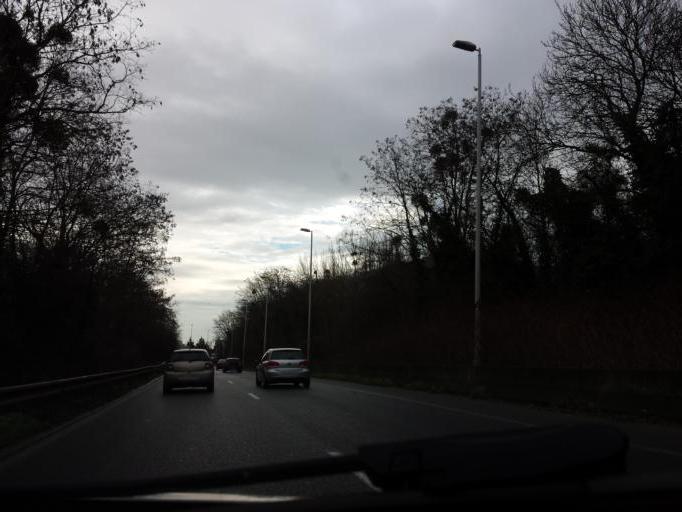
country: FR
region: Ile-de-France
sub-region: Departement du Val-d'Oise
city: Sannois
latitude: 48.9748
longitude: 2.2422
